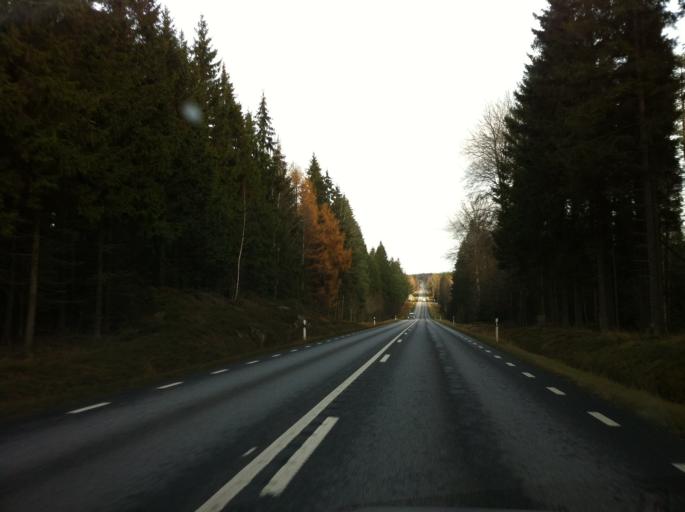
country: SE
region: Kronoberg
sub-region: Alvesta Kommun
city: Vislanda
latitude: 56.7675
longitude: 14.5312
